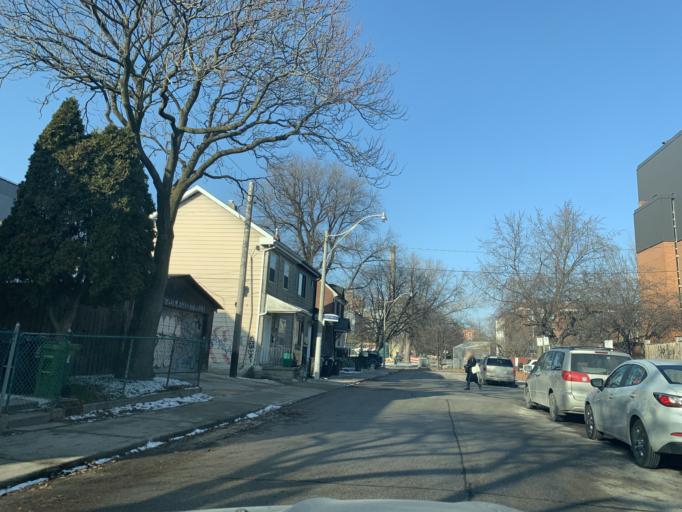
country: CA
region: Ontario
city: Toronto
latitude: 43.6496
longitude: -79.4027
